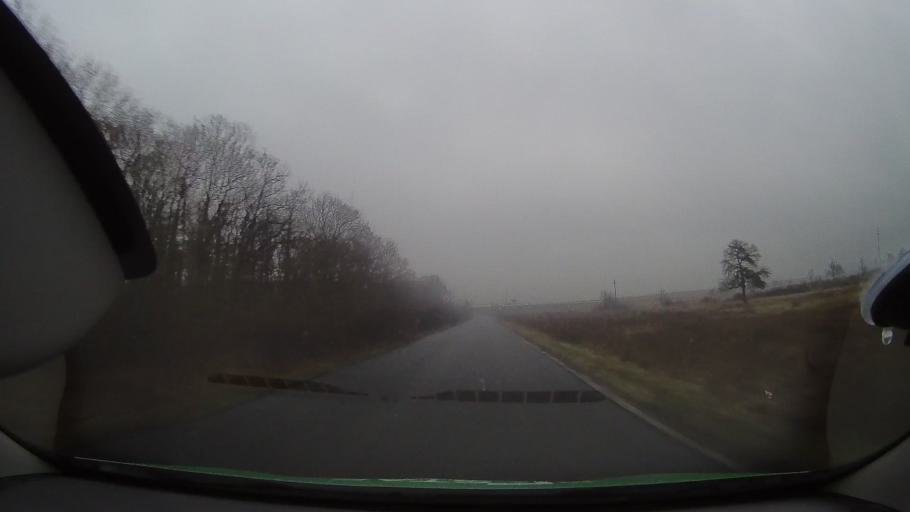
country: RO
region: Bihor
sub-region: Comuna Tinca
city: Gurbediu
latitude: 46.7766
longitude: 21.8794
